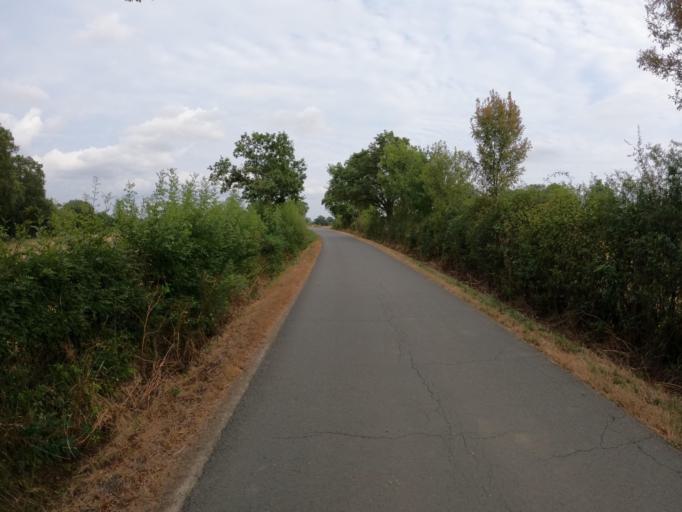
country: FR
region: Pays de la Loire
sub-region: Departement de Maine-et-Loire
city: La Romagne
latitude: 47.0464
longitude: -0.9921
